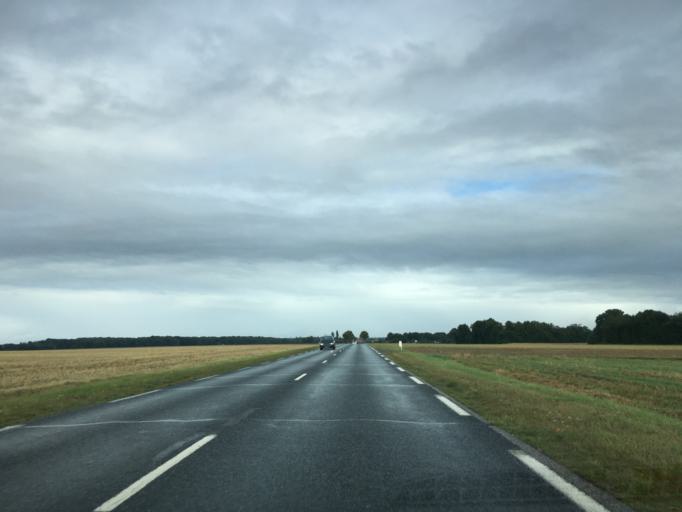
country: FR
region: Haute-Normandie
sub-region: Departement de l'Eure
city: Francheville
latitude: 48.7437
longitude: 0.8481
